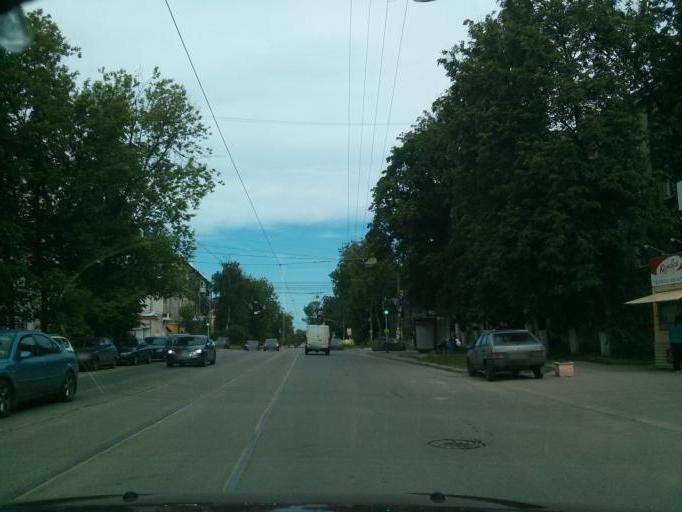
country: RU
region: Nizjnij Novgorod
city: Nizhniy Novgorod
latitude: 56.3116
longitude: 44.0159
